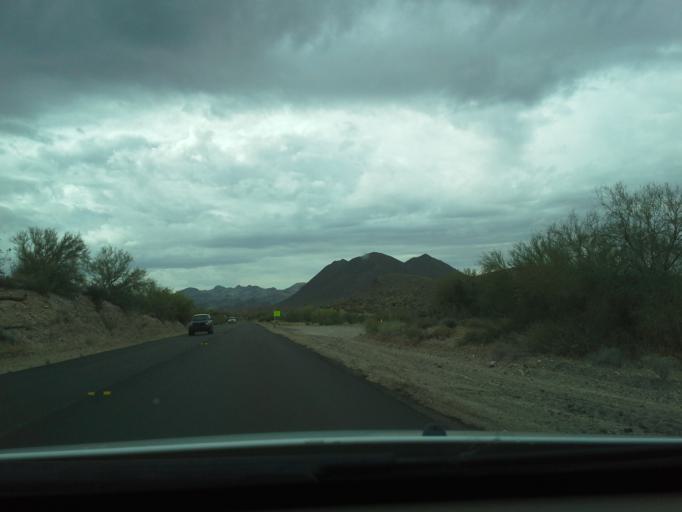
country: US
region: Arizona
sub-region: Maricopa County
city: Rio Verde
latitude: 33.6228
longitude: -111.5567
